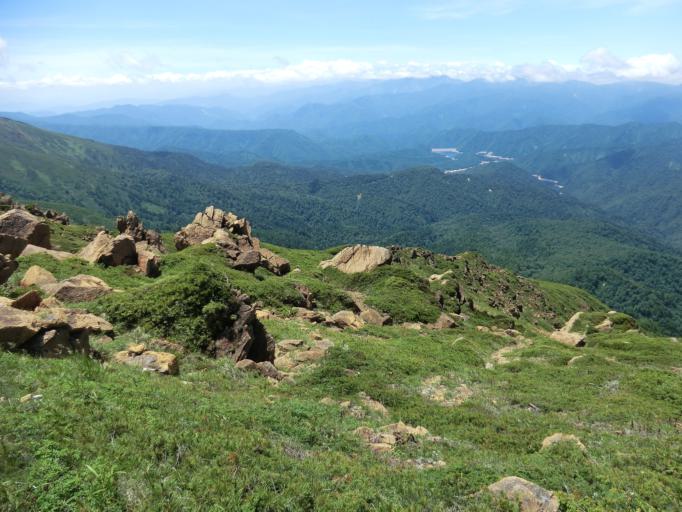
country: JP
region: Gunma
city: Numata
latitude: 36.9007
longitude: 139.1714
